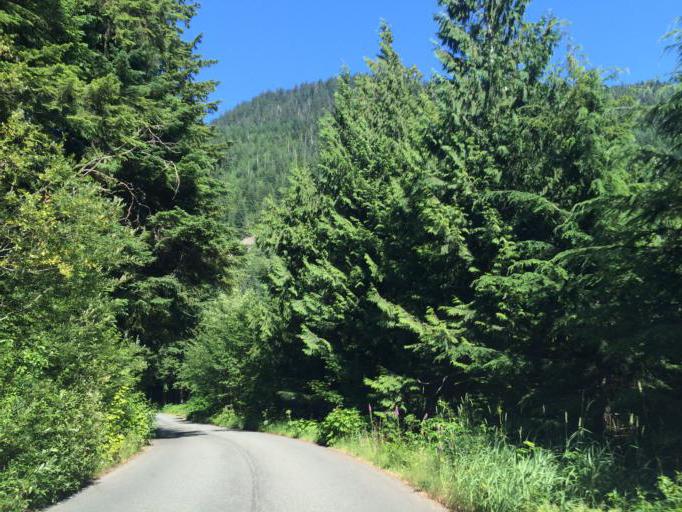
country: US
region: Washington
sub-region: King County
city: Tanner
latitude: 47.4007
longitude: -121.4487
